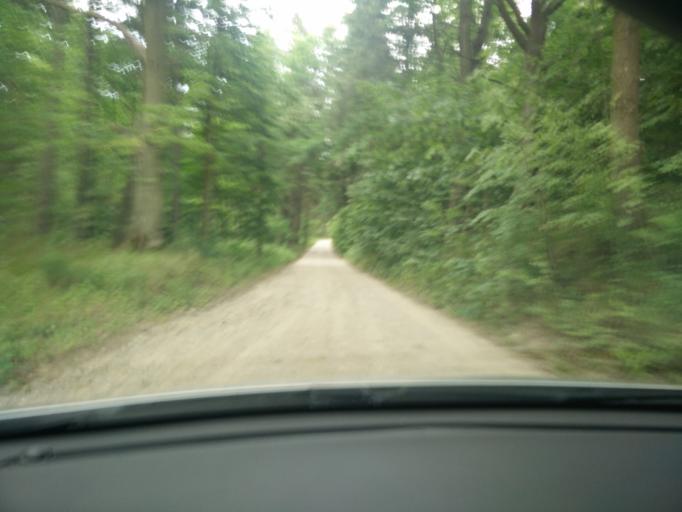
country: PL
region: Pomeranian Voivodeship
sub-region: Powiat pucki
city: Mrzezino
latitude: 54.6579
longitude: 18.4406
